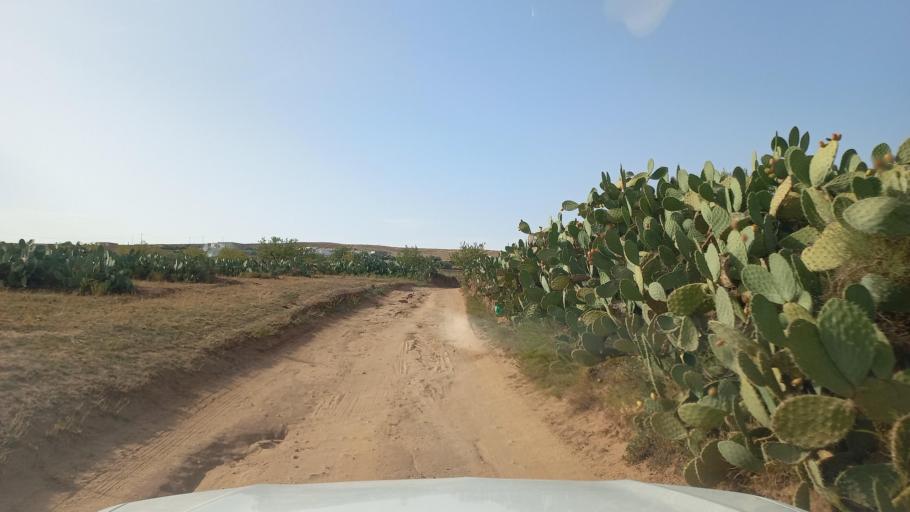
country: TN
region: Al Qasrayn
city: Kasserine
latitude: 35.3618
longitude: 8.8504
